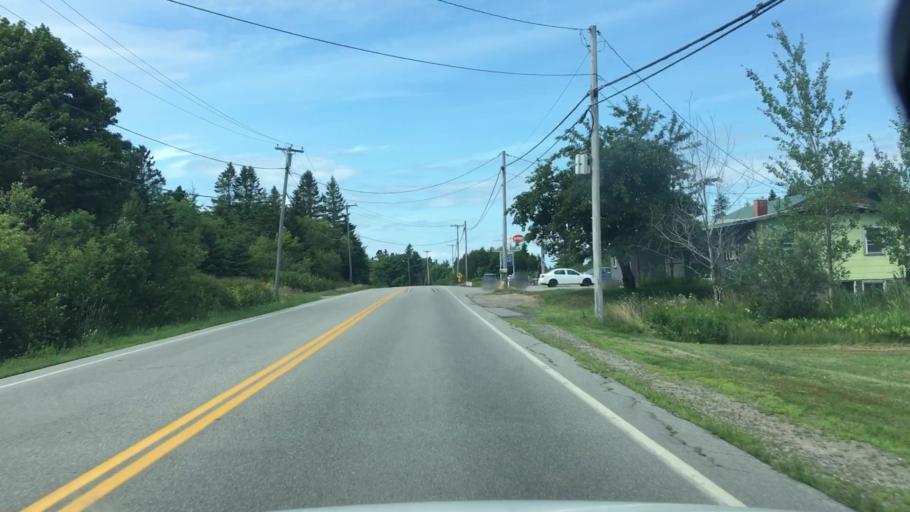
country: US
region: Maine
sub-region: Washington County
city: Eastport
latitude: 44.9100
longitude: -66.9991
